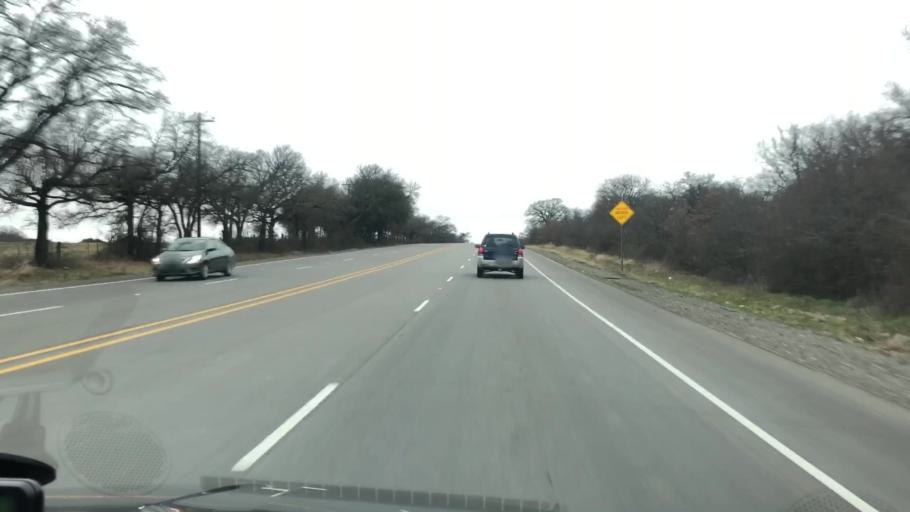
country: US
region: Texas
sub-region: Hamilton County
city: Hico
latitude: 32.0087
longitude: -98.0594
